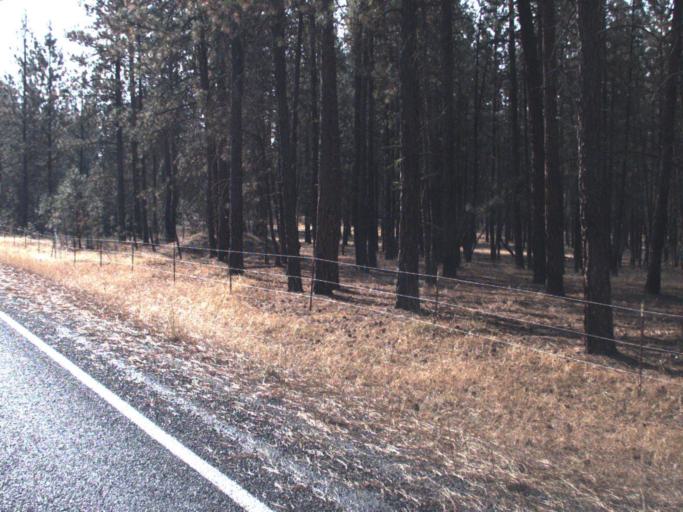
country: US
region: Washington
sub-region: Spokane County
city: Fairchild Air Force Base
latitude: 47.8458
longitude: -117.8502
